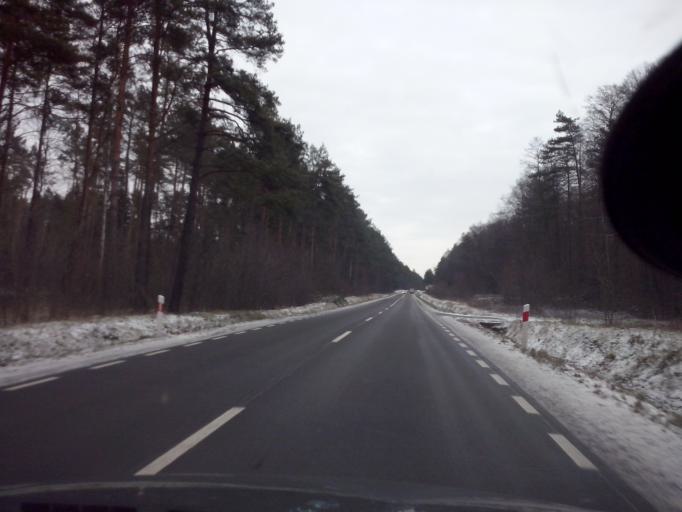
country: PL
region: Lublin Voivodeship
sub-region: Powiat bilgorajski
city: Bilgoraj
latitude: 50.5612
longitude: 22.7719
